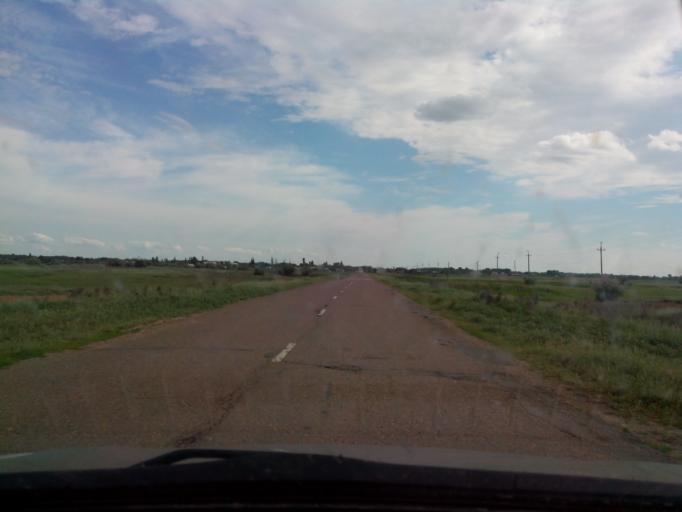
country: RU
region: Volgograd
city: Leninsk
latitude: 48.6801
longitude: 45.3704
